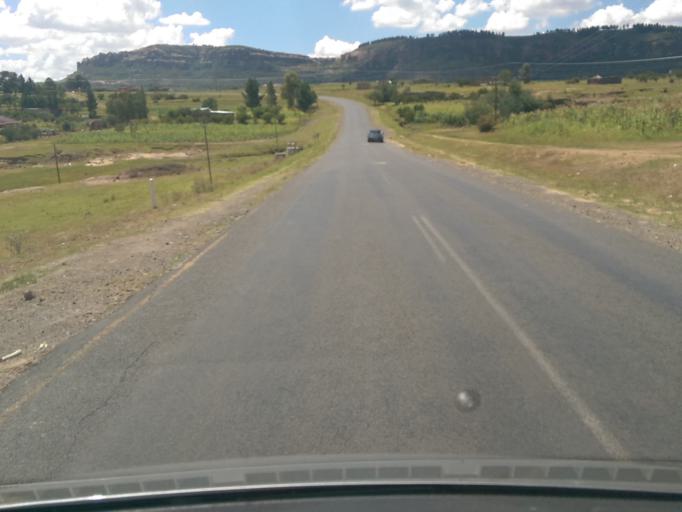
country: LS
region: Maseru
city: Nako
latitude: -29.4292
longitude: 27.6758
